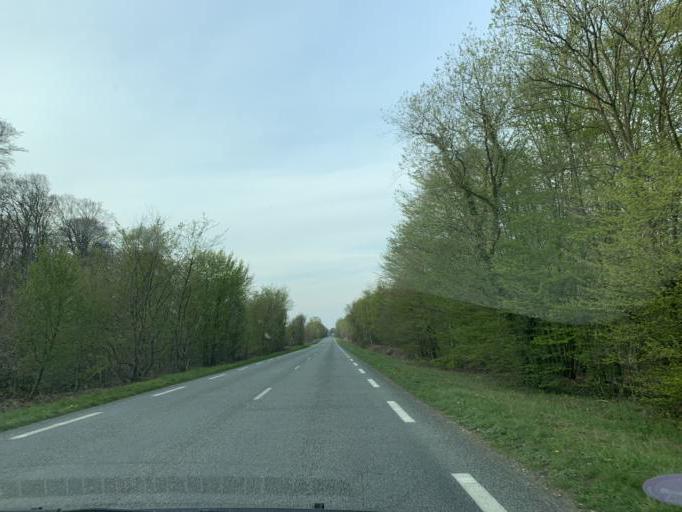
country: FR
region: Haute-Normandie
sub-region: Departement de la Seine-Maritime
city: La Mailleraye-sur-Seine
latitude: 49.4524
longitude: 0.7853
